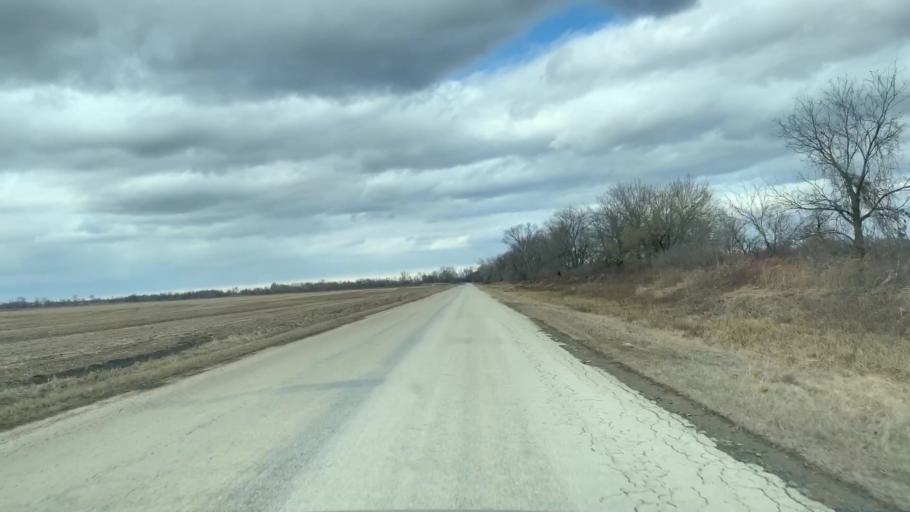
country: US
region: Kansas
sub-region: Allen County
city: Humboldt
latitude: 37.7922
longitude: -95.4706
